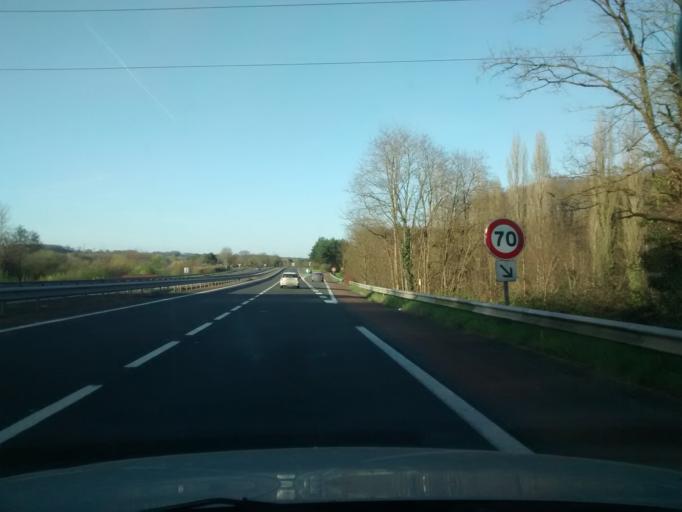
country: FR
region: Pays de la Loire
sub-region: Departement de la Sarthe
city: Change
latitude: 47.9941
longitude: 0.2857
